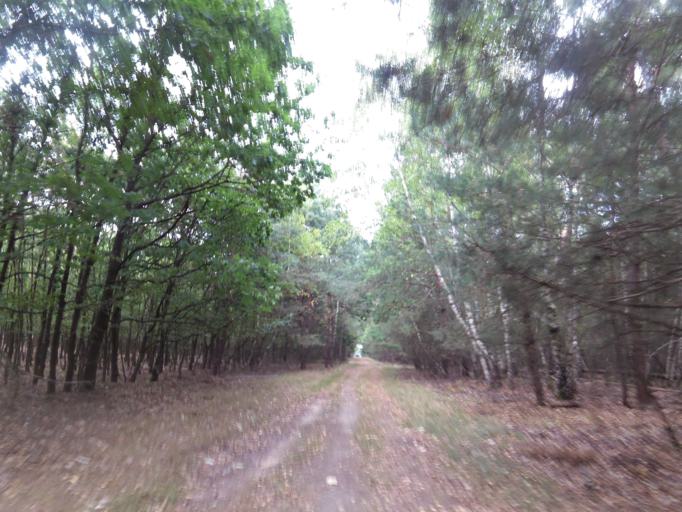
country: DE
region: Hesse
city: Morfelden-Walldorf
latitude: 50.0219
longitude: 8.5548
